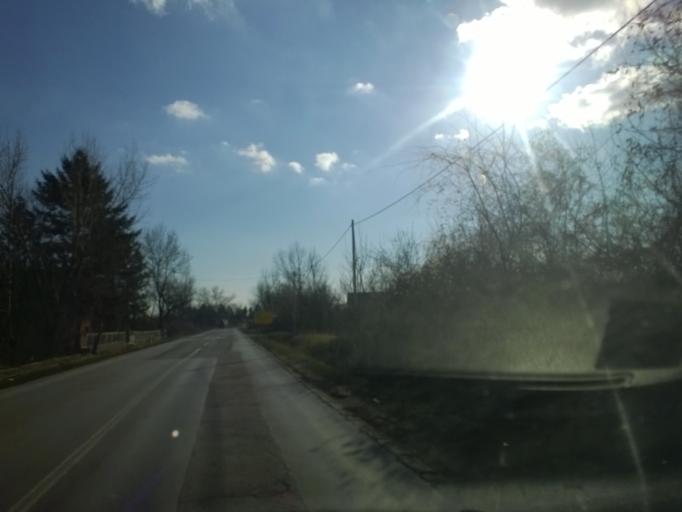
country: RS
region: Central Serbia
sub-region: Podunavski Okrug
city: Smederevo
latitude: 44.5868
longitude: 20.9747
